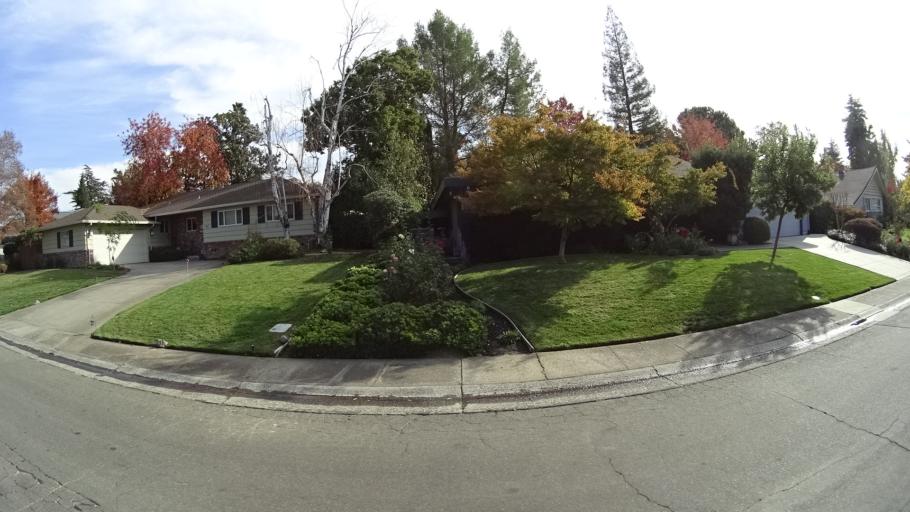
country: US
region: California
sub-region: Sacramento County
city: Fair Oaks
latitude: 38.6676
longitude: -121.2796
